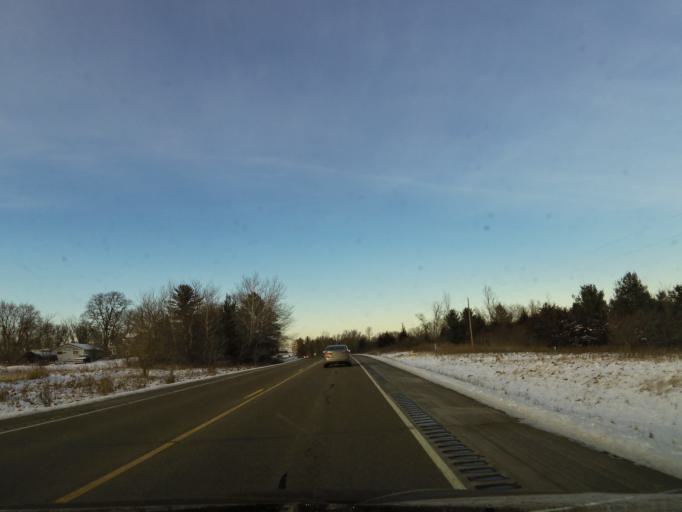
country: US
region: Wisconsin
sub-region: Polk County
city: Osceola
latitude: 45.3566
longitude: -92.7127
